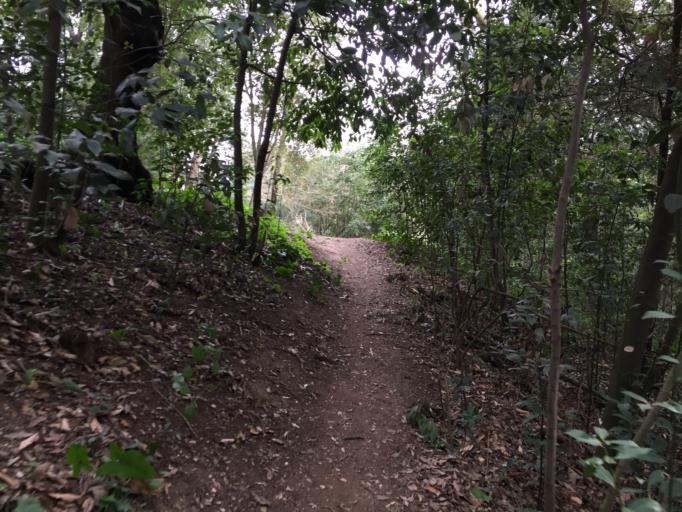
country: VA
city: Vatican City
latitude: 41.8842
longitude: 12.4456
